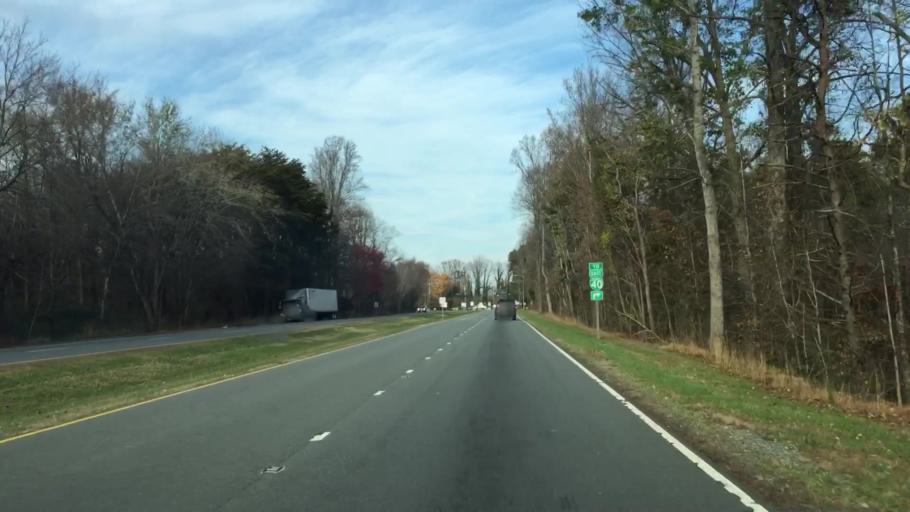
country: US
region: North Carolina
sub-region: Forsyth County
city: Winston-Salem
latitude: 36.1120
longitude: -80.1886
